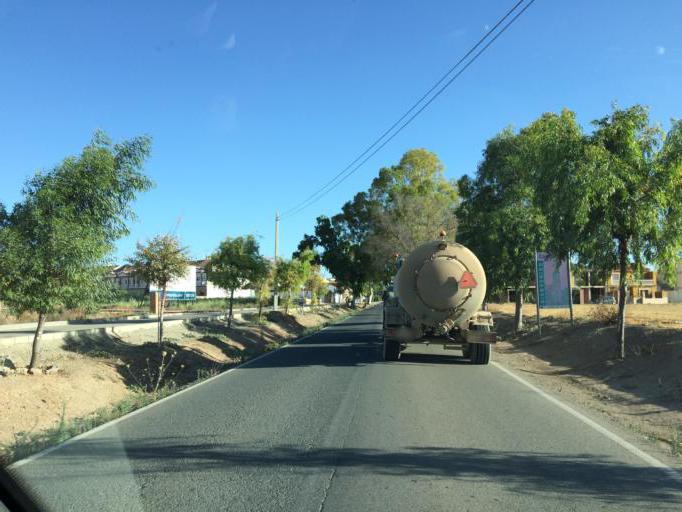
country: ES
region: Andalusia
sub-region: Provincia de Malaga
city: Campillos
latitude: 37.0400
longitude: -4.8590
